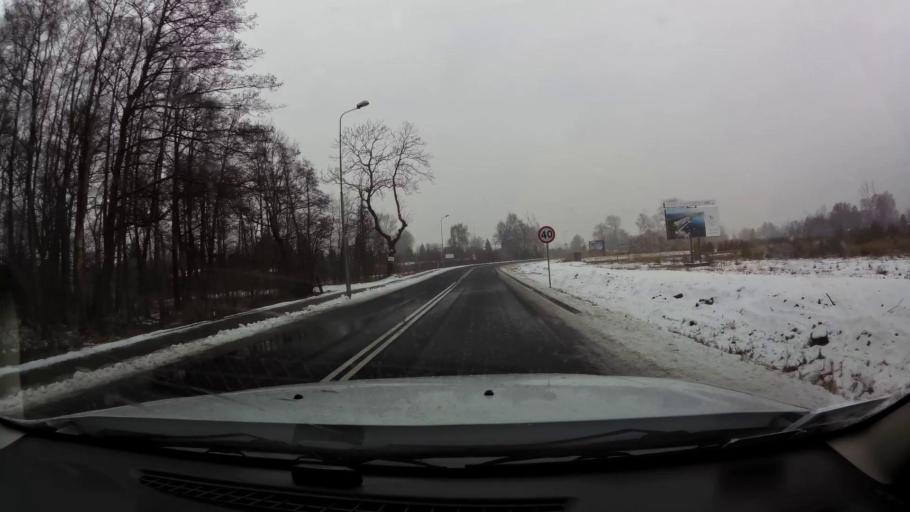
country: PL
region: West Pomeranian Voivodeship
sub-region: Powiat gryficki
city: Mrzezyno
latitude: 54.1380
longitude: 15.2858
